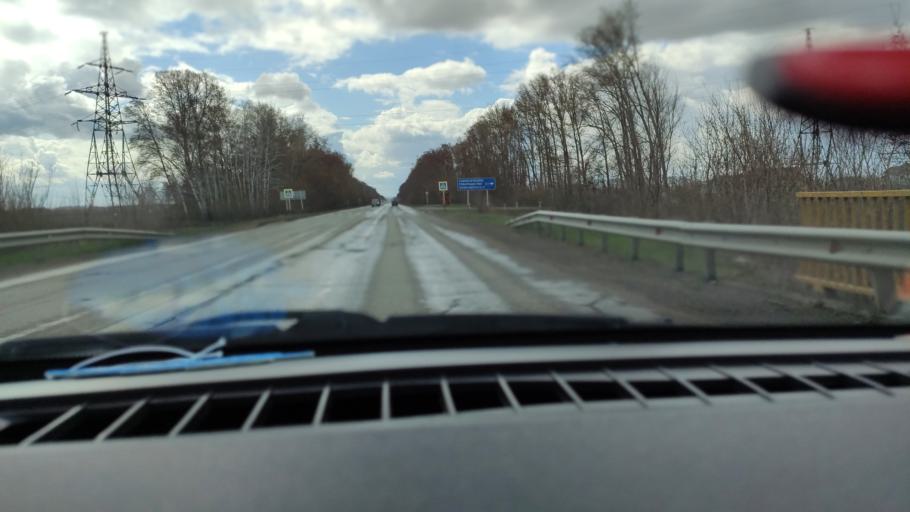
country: RU
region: Samara
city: Tol'yatti
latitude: 53.6275
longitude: 49.4164
